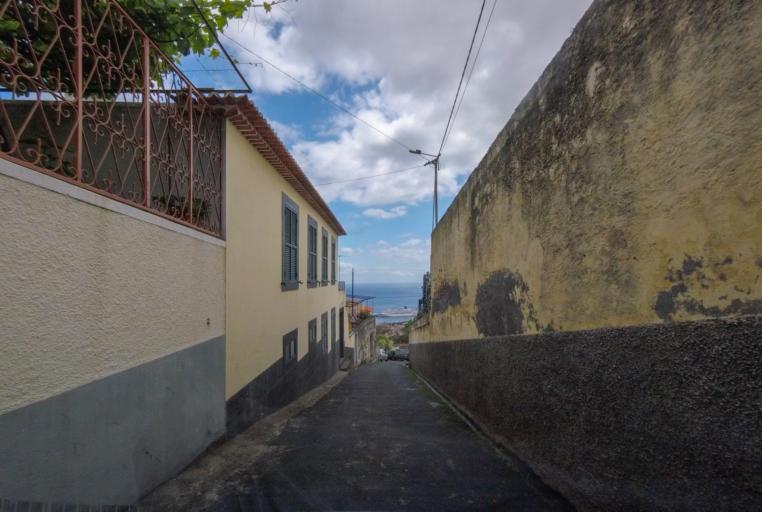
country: PT
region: Madeira
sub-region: Funchal
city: Nossa Senhora do Monte
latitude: 32.6607
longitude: -16.9055
